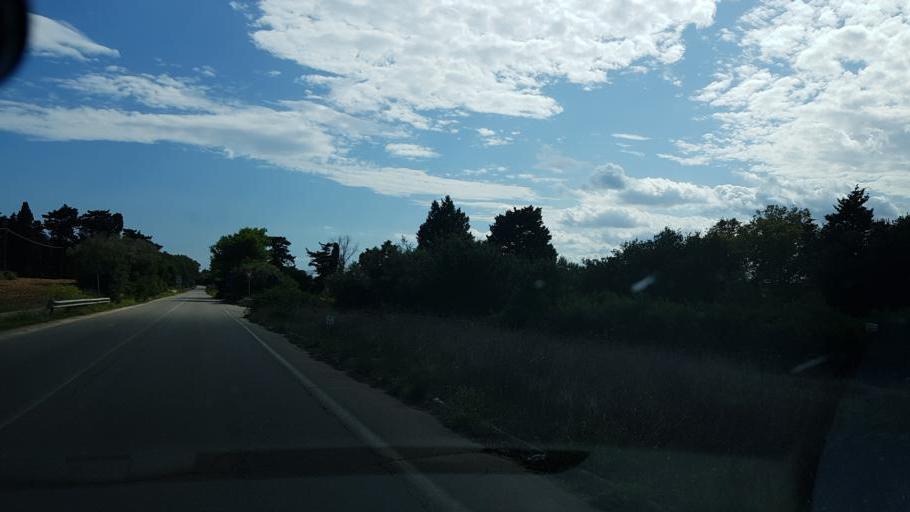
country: IT
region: Apulia
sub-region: Provincia di Lecce
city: Borgagne
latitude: 40.2229
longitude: 18.4416
